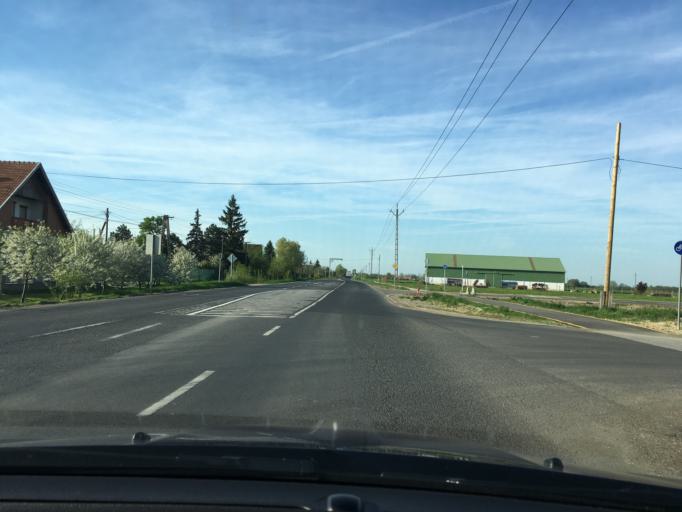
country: HU
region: Bekes
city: Korosladany
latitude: 46.9726
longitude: 21.0889
